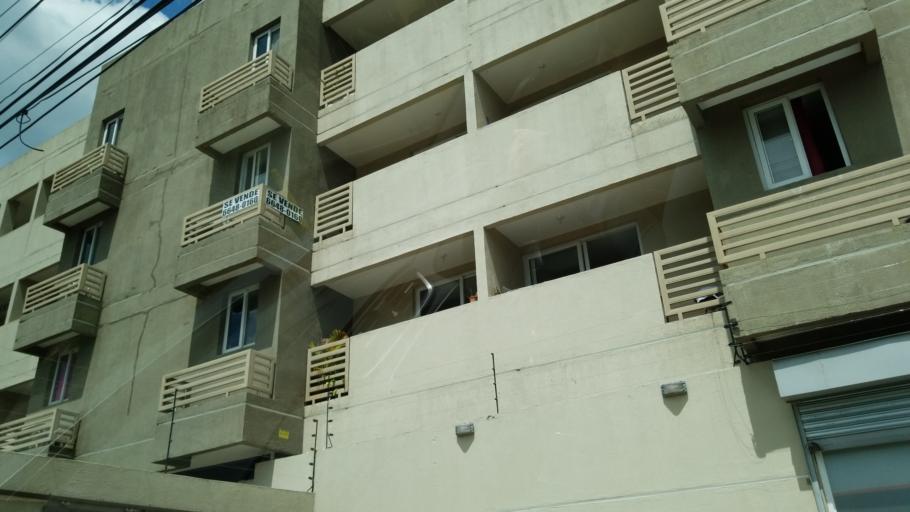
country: PA
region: Panama
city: San Miguelito
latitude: 9.0453
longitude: -79.4314
